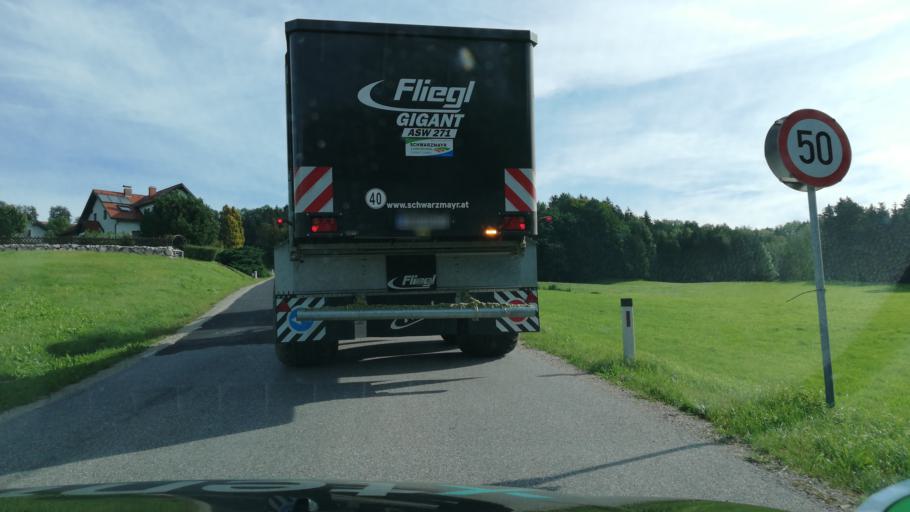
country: AT
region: Lower Austria
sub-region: Politischer Bezirk Amstetten
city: Behamberg
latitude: 48.0394
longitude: 14.4687
